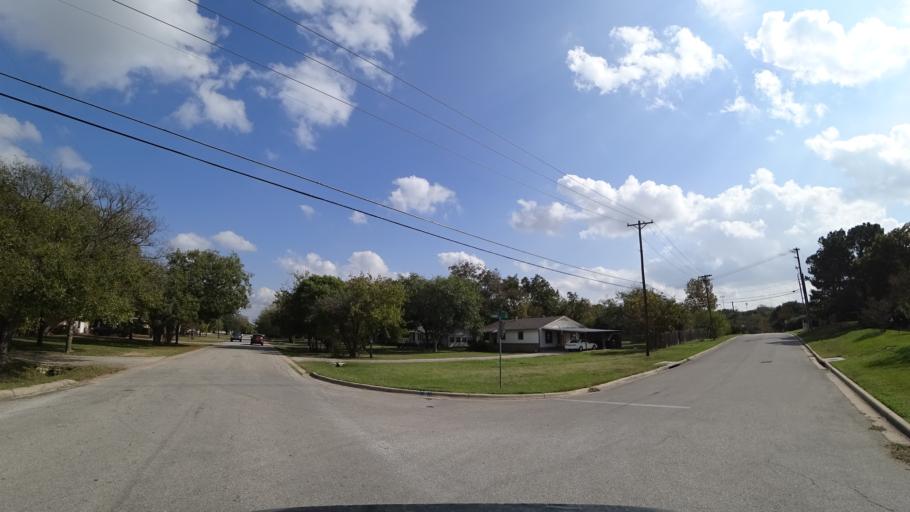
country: US
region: Texas
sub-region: Williamson County
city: Round Rock
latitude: 30.5147
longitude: -97.6850
